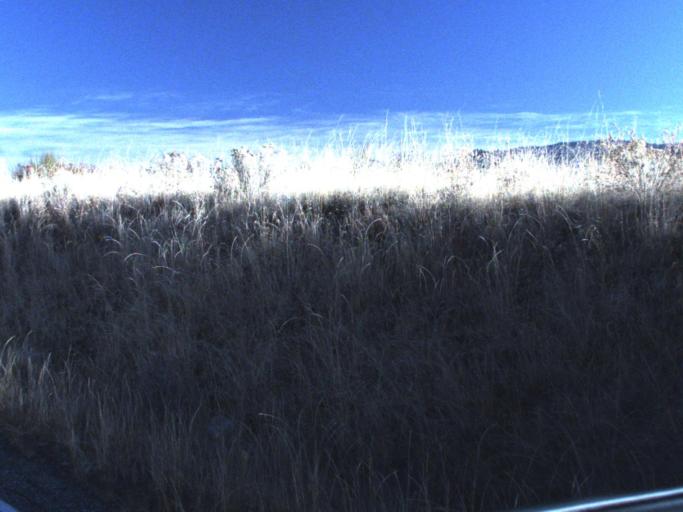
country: US
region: Washington
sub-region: Okanogan County
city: Coulee Dam
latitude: 47.9926
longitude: -118.6932
